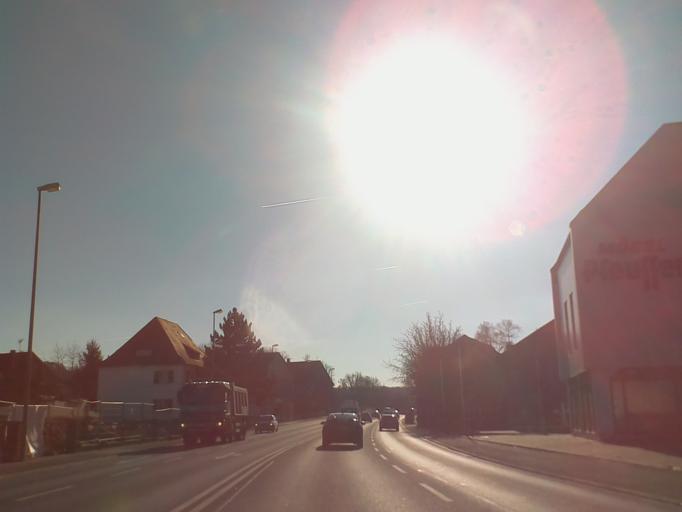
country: DE
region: Bavaria
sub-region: Regierungsbezirk Unterfranken
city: Bad Neustadt an der Saale
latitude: 50.3261
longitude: 10.2209
